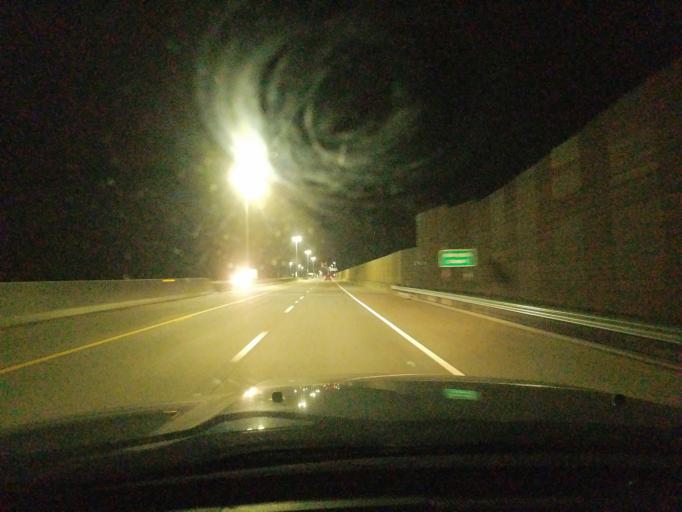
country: US
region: Kentucky
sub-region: Jefferson County
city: Prospect
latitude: 38.3297
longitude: -85.6280
